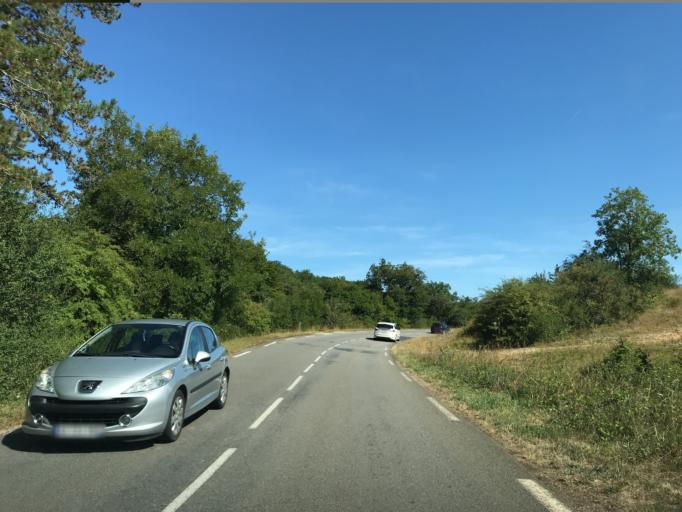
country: FR
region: Limousin
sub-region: Departement de la Correze
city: Larche
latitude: 45.0357
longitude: 1.3751
